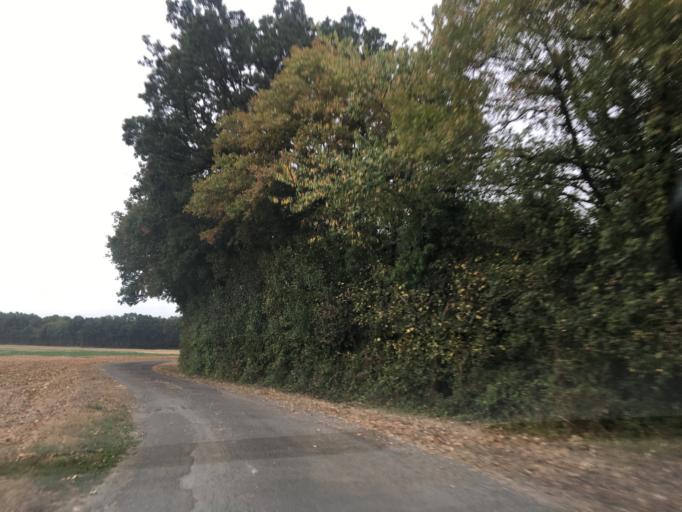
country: FR
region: Poitou-Charentes
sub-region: Departement des Deux-Sevres
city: Beauvoir-sur-Niort
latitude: 46.0841
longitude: -0.5250
